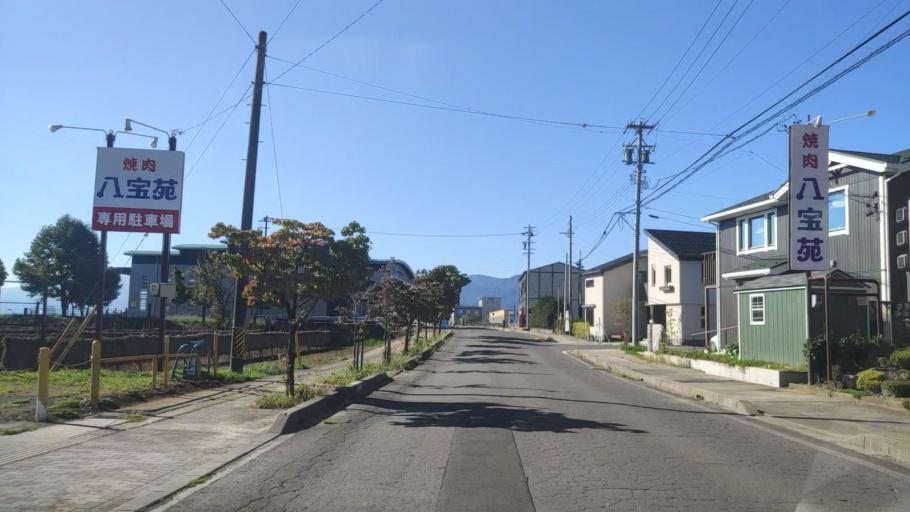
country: JP
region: Nagano
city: Okaya
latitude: 36.0639
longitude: 138.0801
